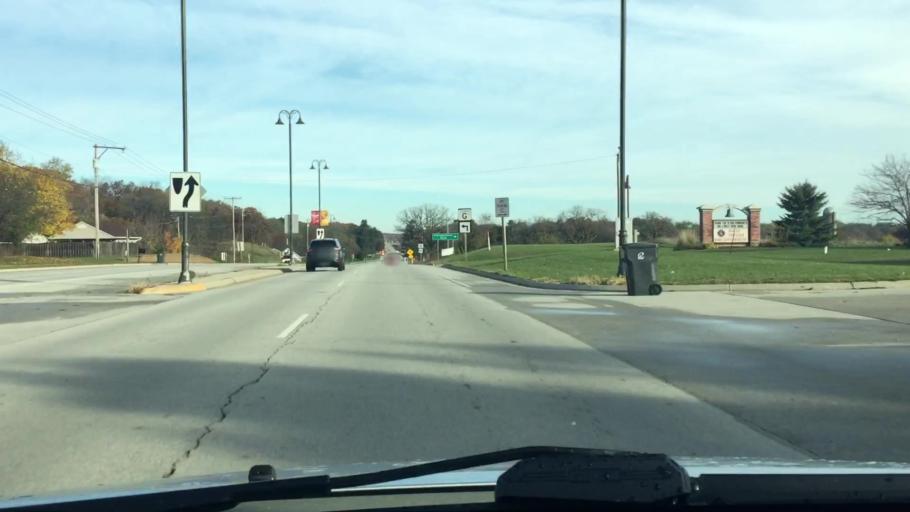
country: US
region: Wisconsin
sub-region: Waukesha County
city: Wales
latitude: 42.9939
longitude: -88.3842
